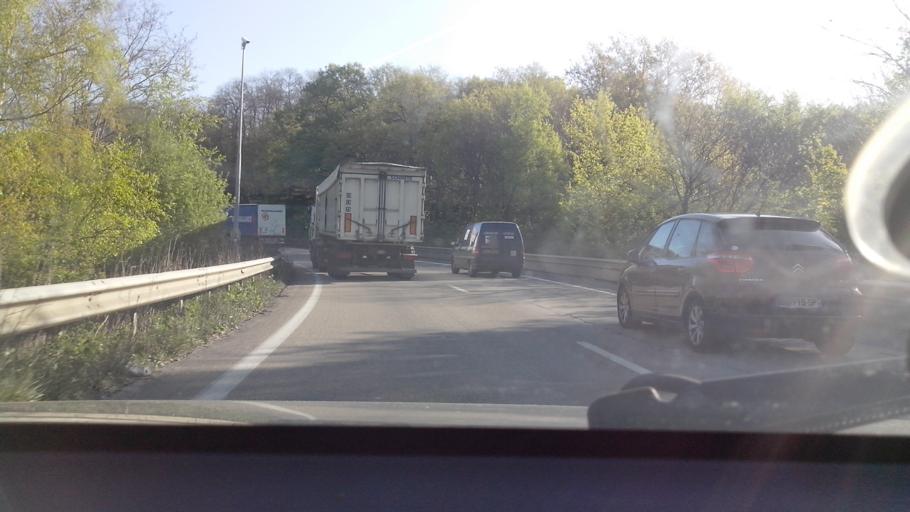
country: FR
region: Ile-de-France
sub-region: Departement de l'Essonne
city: Les Ulis
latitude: 48.6678
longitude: 2.1931
